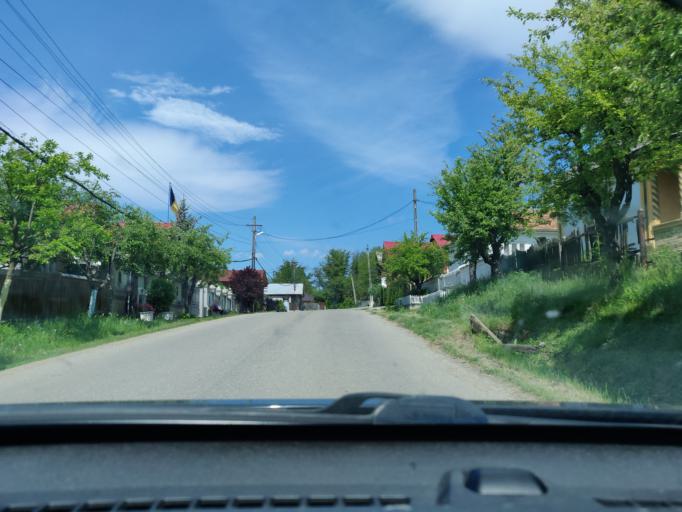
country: RO
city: Vizantea-Manastireasca
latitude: 45.9550
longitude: 26.8318
